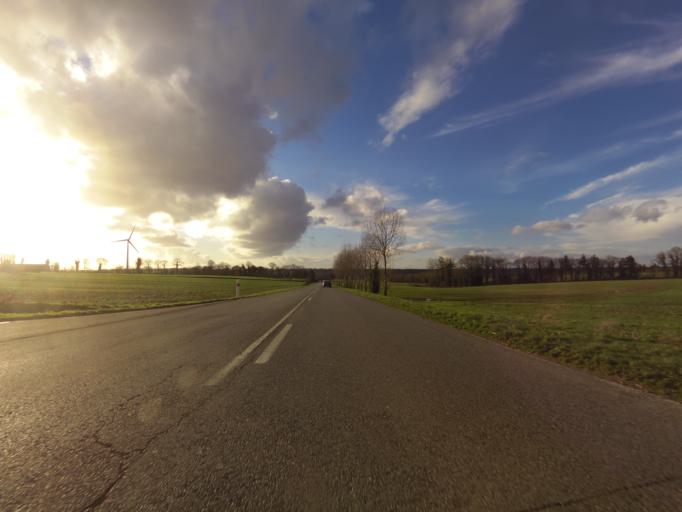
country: FR
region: Brittany
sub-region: Departement du Morbihan
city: Credin
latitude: 48.0088
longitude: -2.7680
